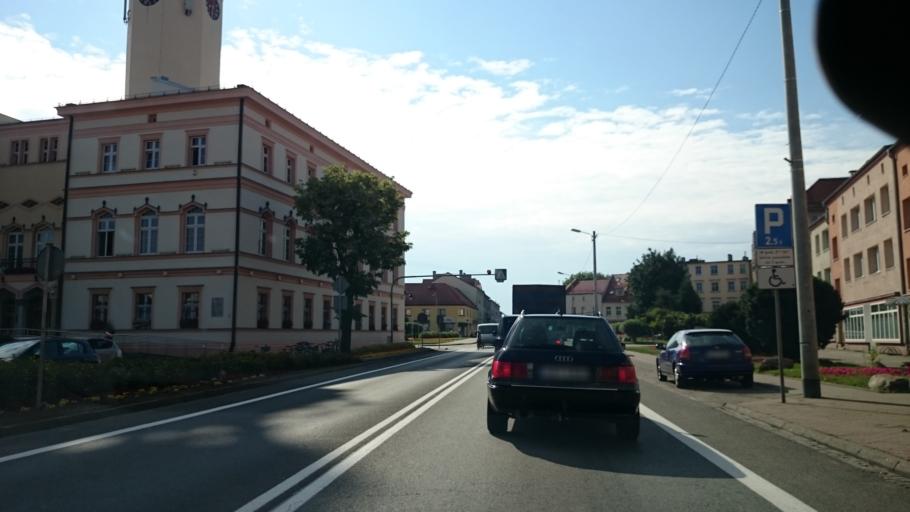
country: PL
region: Opole Voivodeship
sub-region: Powiat strzelecki
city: Strzelce Opolskie
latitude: 50.5109
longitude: 18.2998
